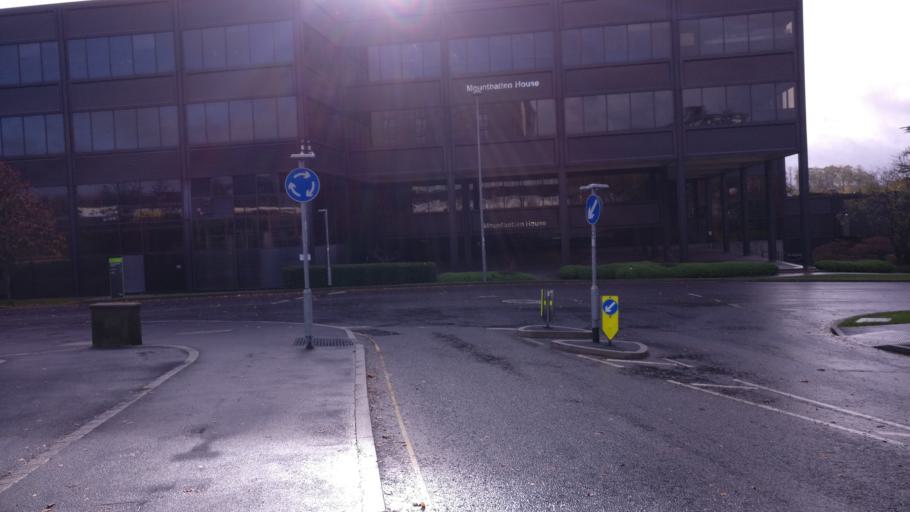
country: GB
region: England
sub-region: Hampshire
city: Basingstoke
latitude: 51.2688
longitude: -1.0745
